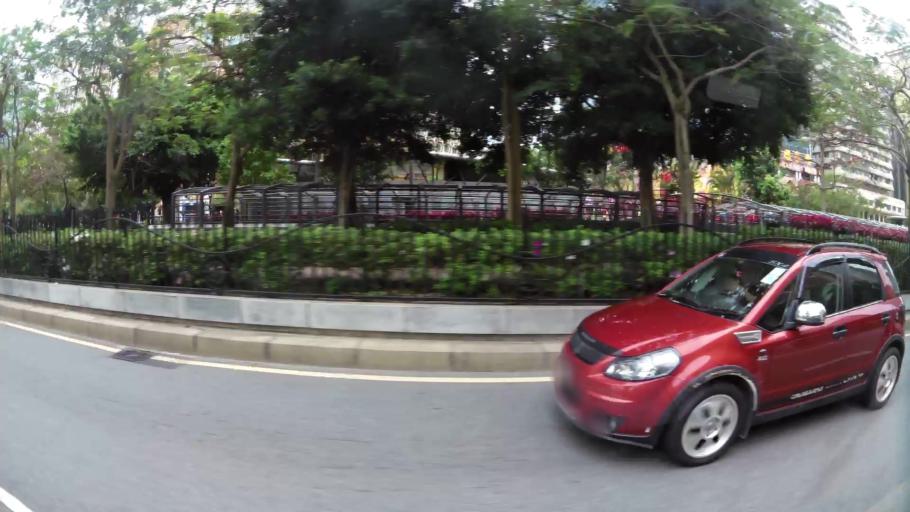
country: MO
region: Macau
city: Macau
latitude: 22.1890
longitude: 113.5455
